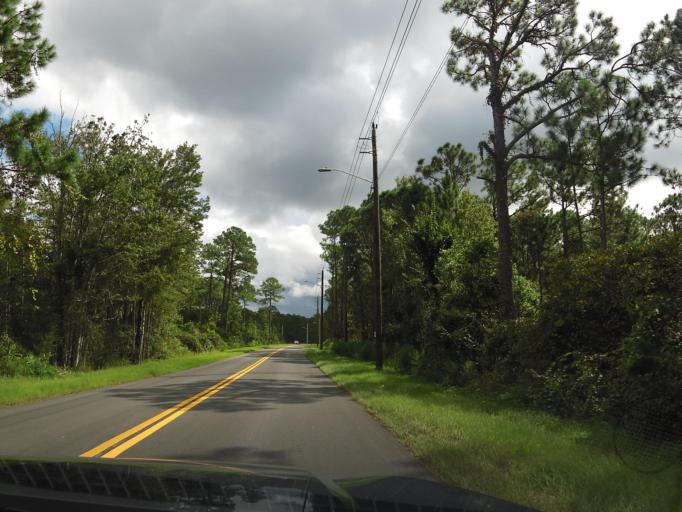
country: US
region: Florida
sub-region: Saint Johns County
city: Palm Valley
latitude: 30.0431
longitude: -81.4156
